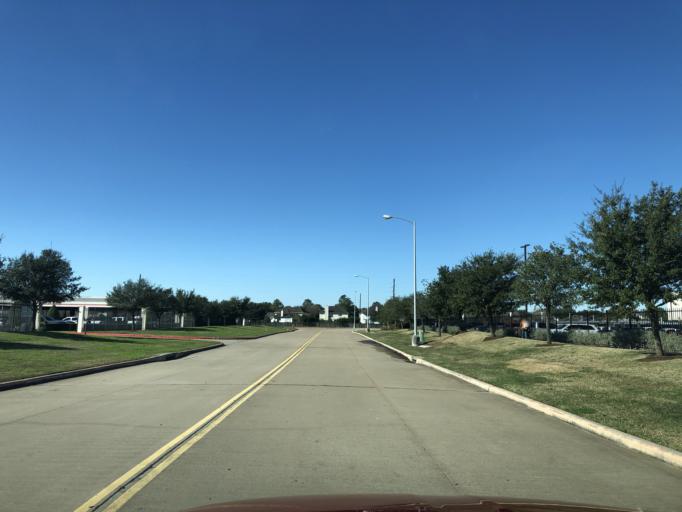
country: US
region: Texas
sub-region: Harris County
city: Oak Cliff Place
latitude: 29.9362
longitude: -95.6572
